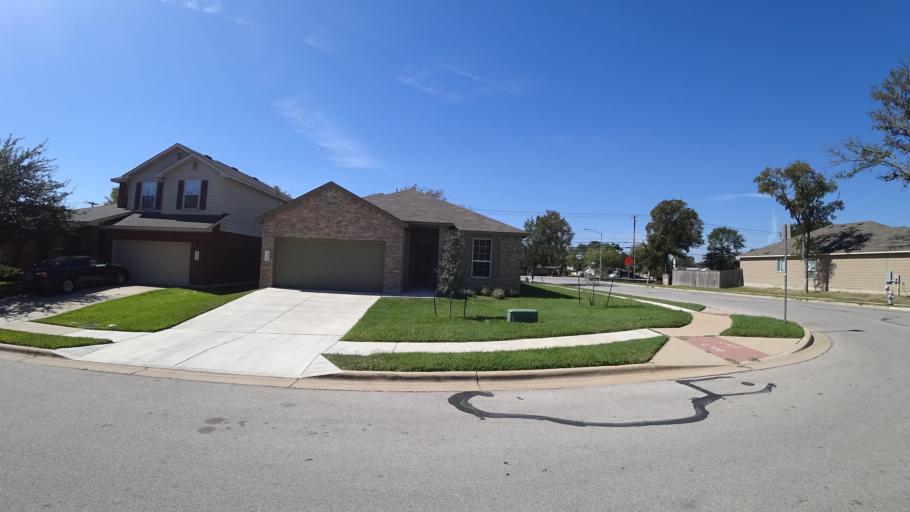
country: US
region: Texas
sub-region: Travis County
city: Hornsby Bend
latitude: 30.2733
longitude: -97.6336
